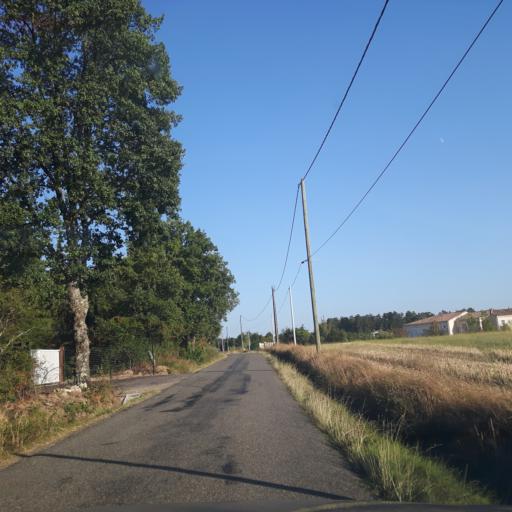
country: FR
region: Midi-Pyrenees
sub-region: Departement de la Haute-Garonne
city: Villaudric
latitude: 43.8002
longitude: 1.4475
